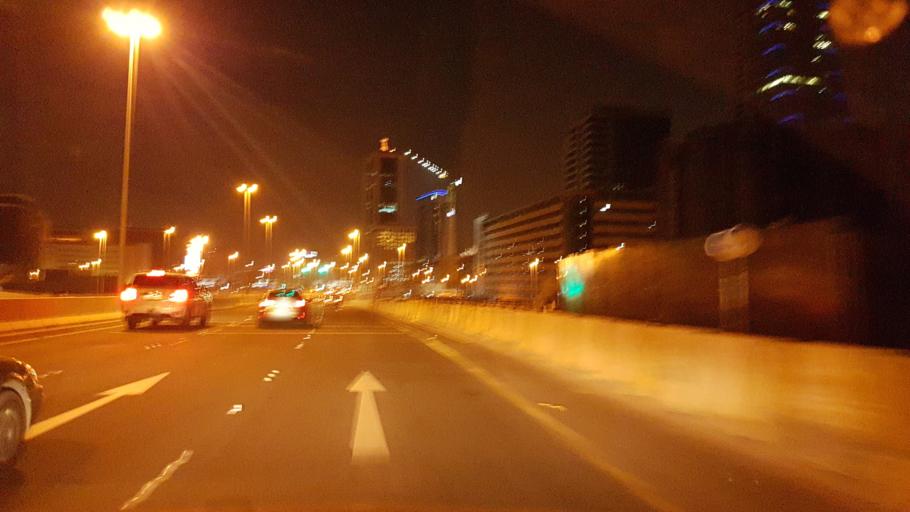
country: BH
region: Manama
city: Manama
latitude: 26.2413
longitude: 50.5747
